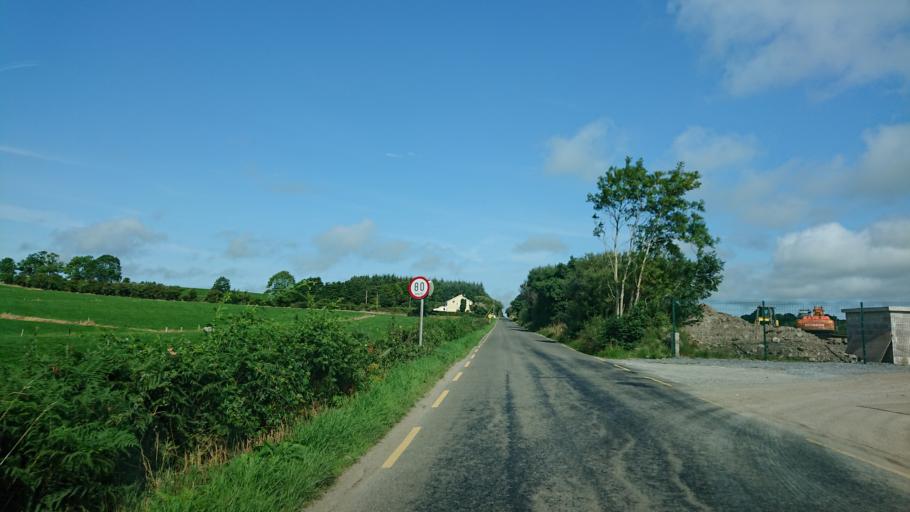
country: IE
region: Munster
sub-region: Ciarrai
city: Cill Airne
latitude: 52.0990
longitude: -9.5431
